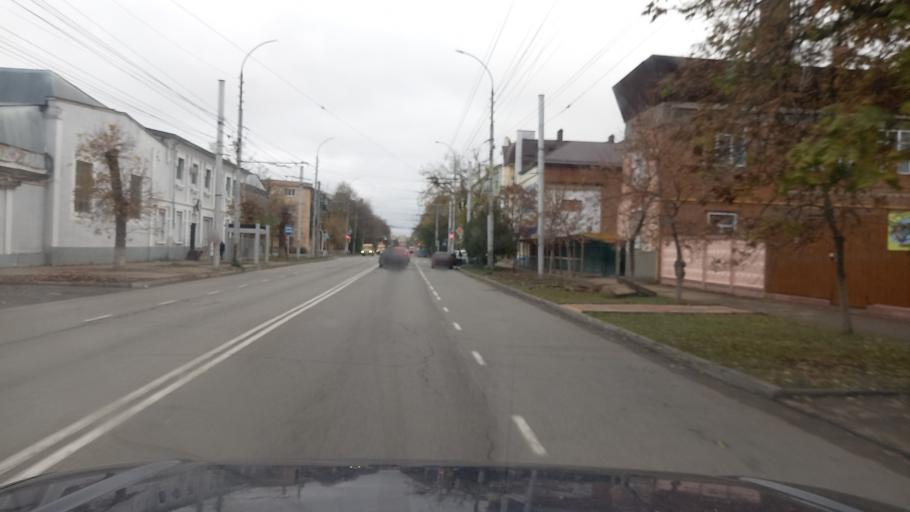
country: RU
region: Adygeya
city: Maykop
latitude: 44.6146
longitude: 40.1087
